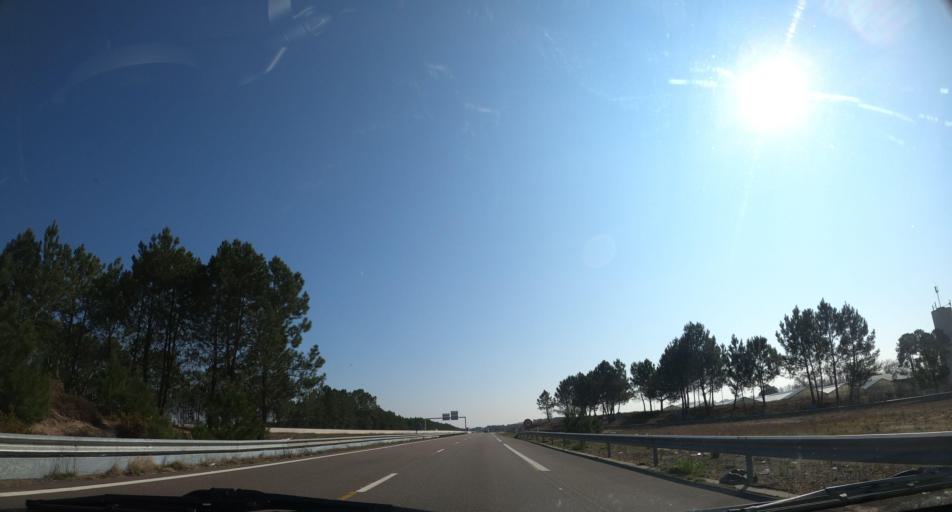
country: FR
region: Aquitaine
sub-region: Departement des Landes
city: Saint-Geours-de-Maremne
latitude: 43.6967
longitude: -1.2260
